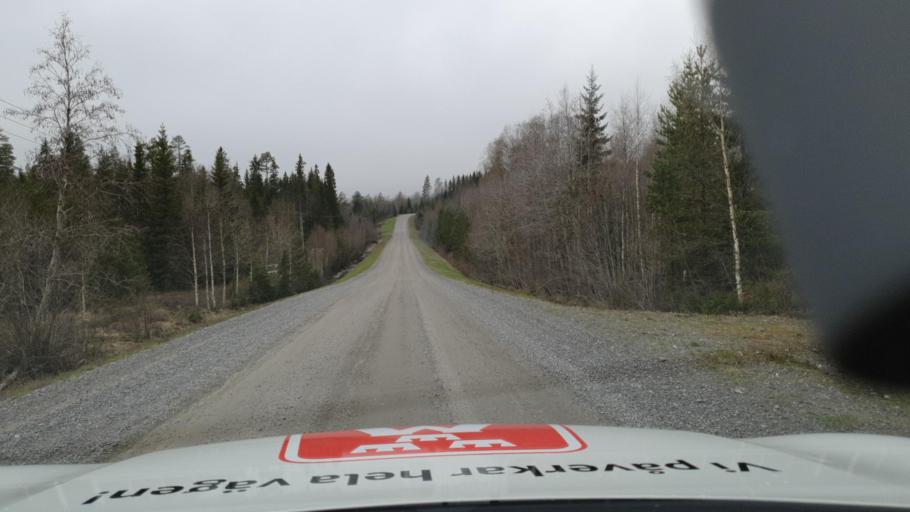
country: SE
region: Vaesterbotten
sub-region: Nordmalings Kommun
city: Nordmaling
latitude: 63.7649
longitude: 19.4540
